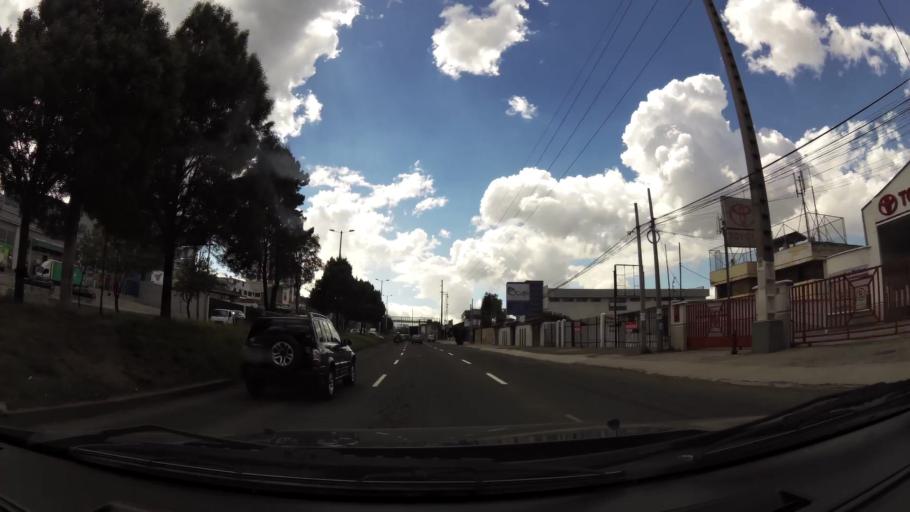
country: EC
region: Pichincha
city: Quito
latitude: -0.1498
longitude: -78.4978
